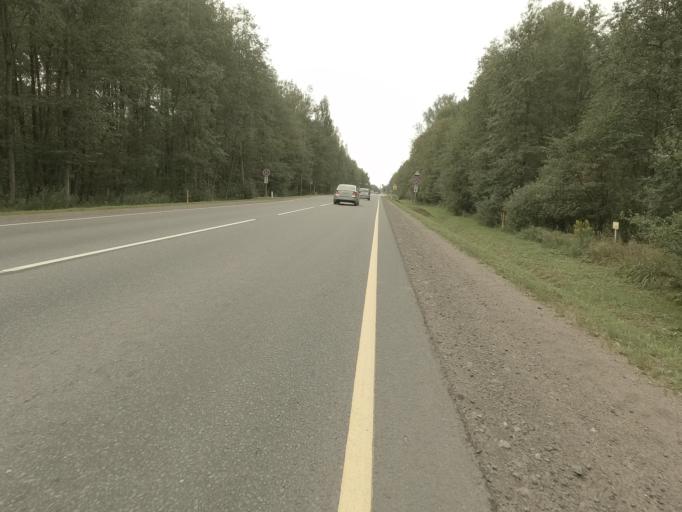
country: RU
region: Leningrad
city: Kirovsk
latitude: 59.8507
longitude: 31.0275
